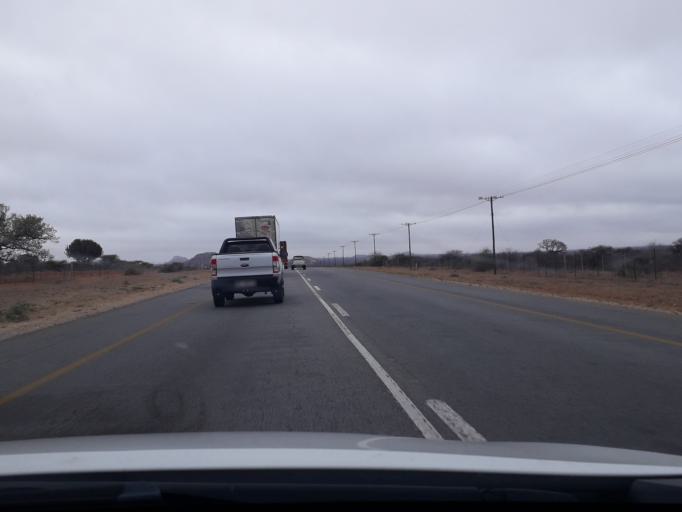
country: ZA
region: Limpopo
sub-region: Capricorn District Municipality
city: Mankoeng
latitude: -23.5613
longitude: 29.6828
